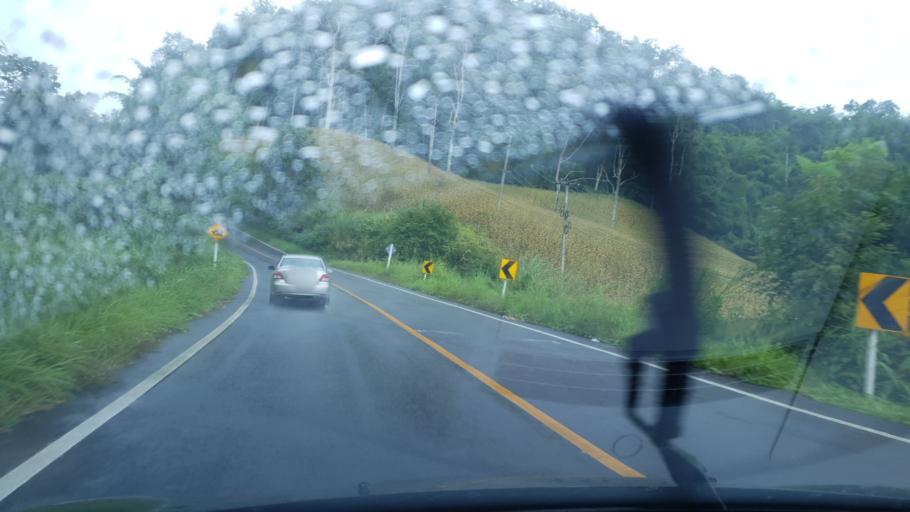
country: TH
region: Mae Hong Son
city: Khun Yuam
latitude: 18.6741
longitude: 97.9244
